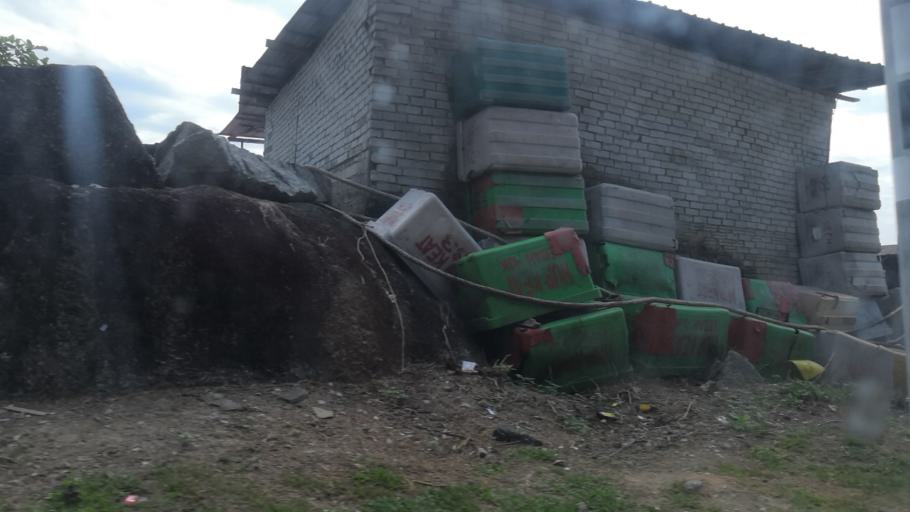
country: MY
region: Perak
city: Lumut
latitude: 4.2166
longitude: 100.5760
